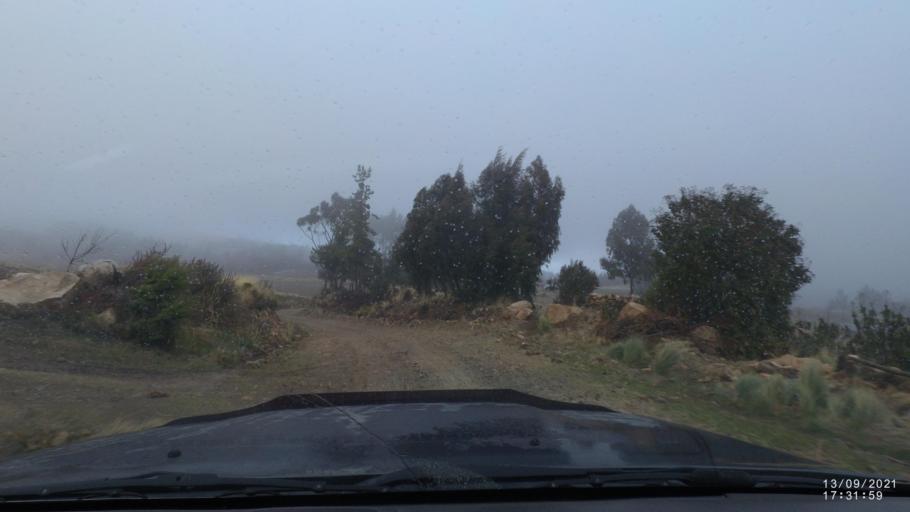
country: BO
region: Cochabamba
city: Colomi
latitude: -17.3660
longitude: -65.7866
